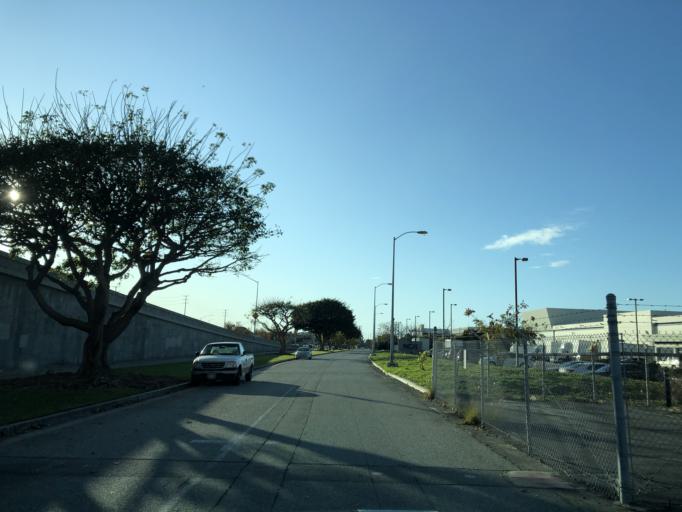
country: US
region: California
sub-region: Los Angeles County
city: El Segundo
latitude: 33.9319
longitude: -118.4001
